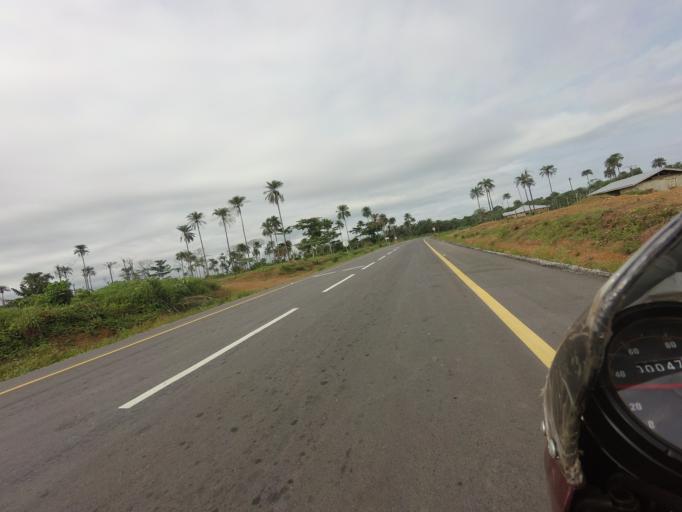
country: SL
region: Eastern Province
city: Mobai
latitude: 8.0124
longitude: -10.7431
